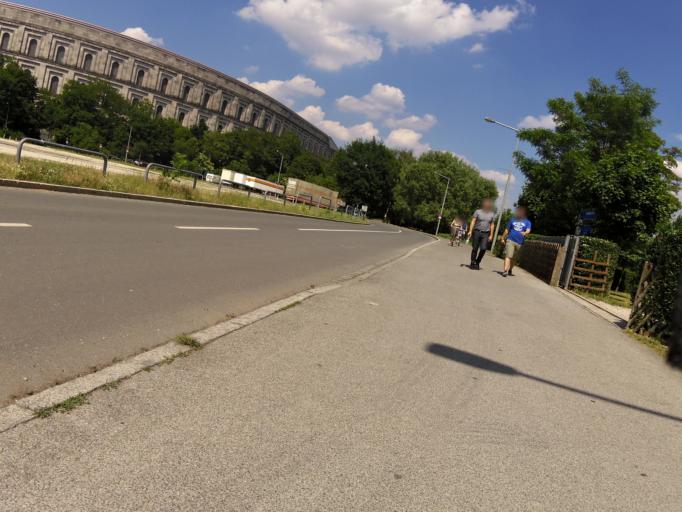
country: DE
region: Bavaria
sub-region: Regierungsbezirk Mittelfranken
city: Nuernberg
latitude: 49.4298
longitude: 11.1121
